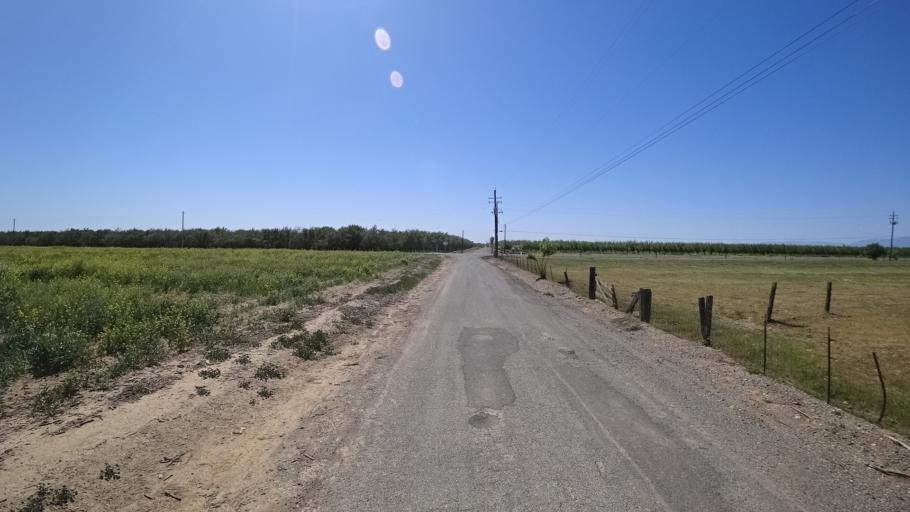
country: US
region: California
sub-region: Glenn County
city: Orland
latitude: 39.6972
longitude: -122.1638
